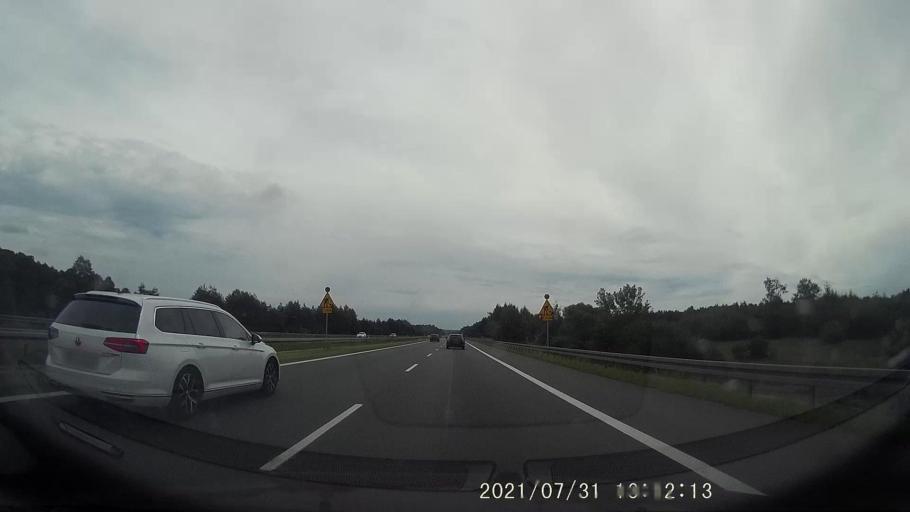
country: PL
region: Lesser Poland Voivodeship
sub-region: Powiat chrzanowski
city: Bolecin
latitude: 50.1245
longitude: 19.4871
